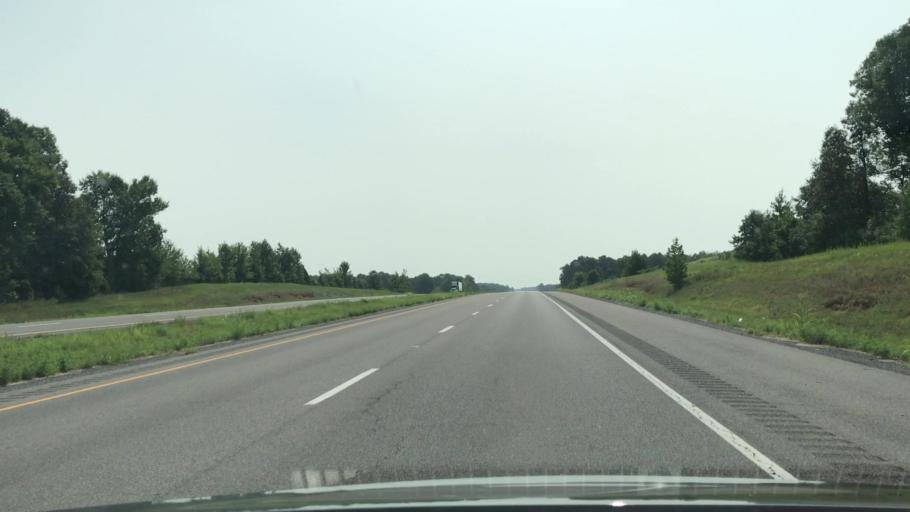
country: US
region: Kentucky
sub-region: Graves County
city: Mayfield
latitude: 36.6718
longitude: -88.5057
